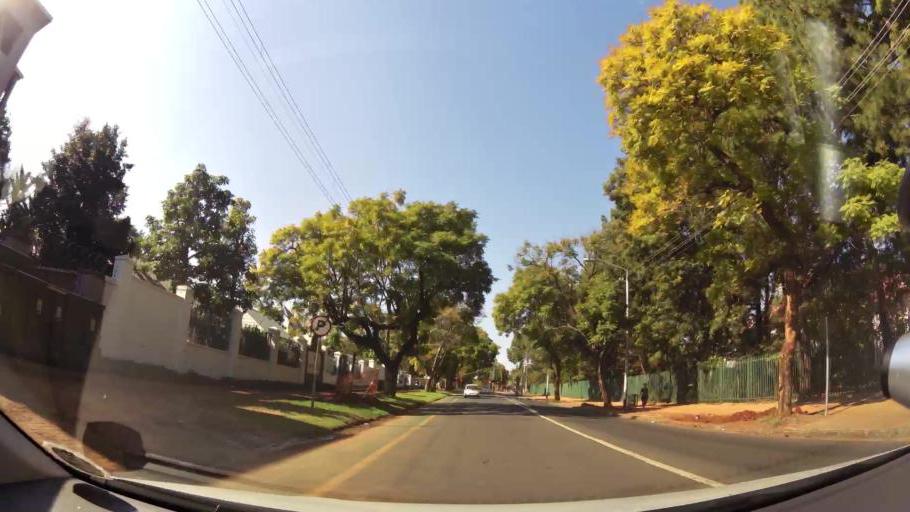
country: ZA
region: Gauteng
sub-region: City of Tshwane Metropolitan Municipality
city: Pretoria
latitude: -25.7497
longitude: 28.2263
